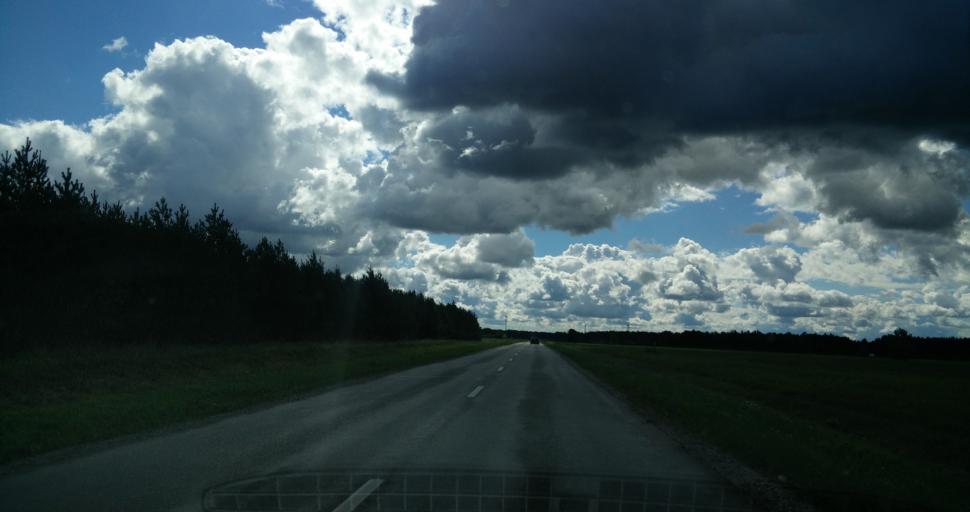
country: LT
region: Klaipedos apskritis
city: Silute
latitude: 55.3231
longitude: 21.5269
